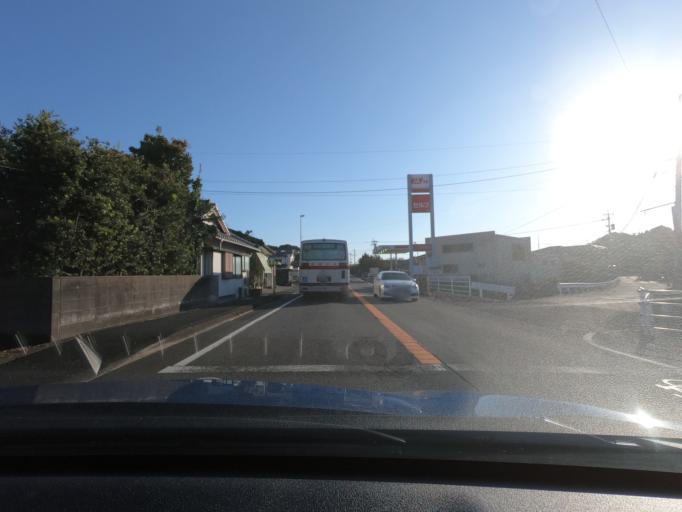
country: JP
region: Kagoshima
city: Akune
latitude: 31.9822
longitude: 130.2037
